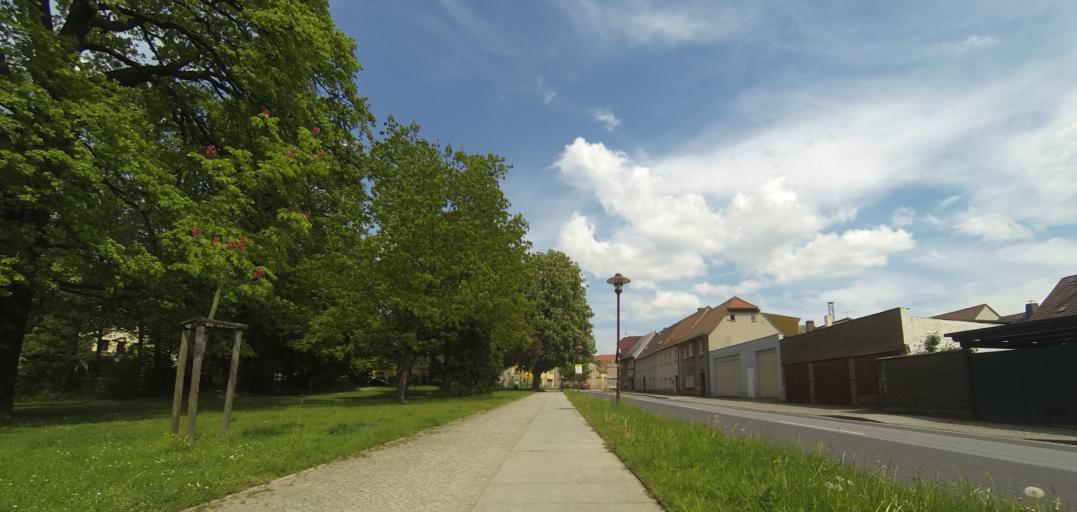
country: DE
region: Saxony
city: Bischofswerda
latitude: 51.1282
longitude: 14.1770
